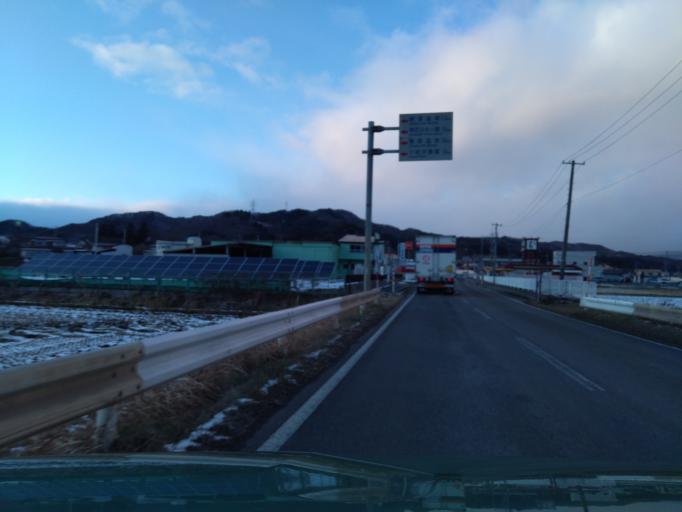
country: JP
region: Iwate
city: Shizukuishi
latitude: 39.6984
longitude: 141.0630
